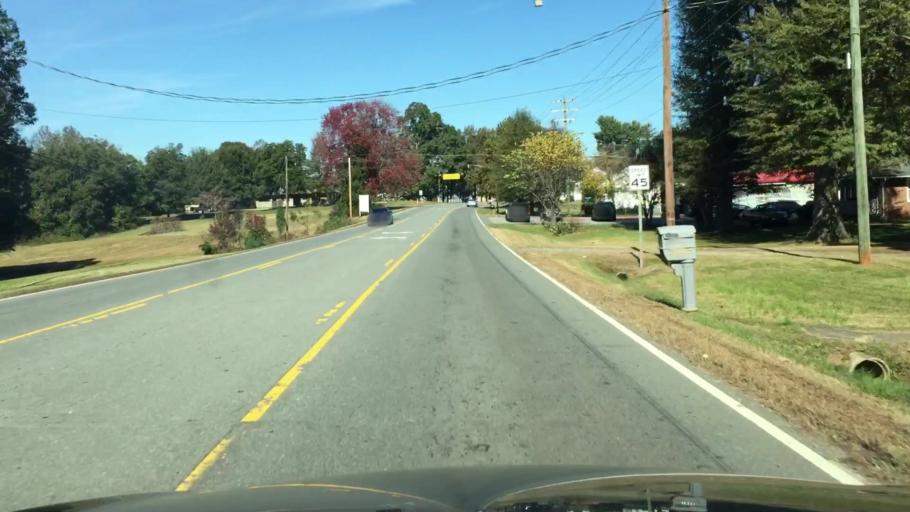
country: US
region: North Carolina
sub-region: Rockingham County
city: Reidsville
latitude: 36.3334
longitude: -79.6519
